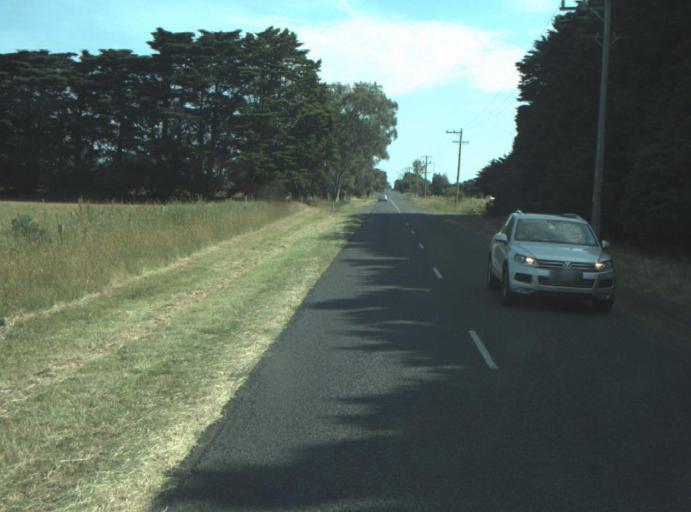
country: AU
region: Victoria
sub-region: Greater Geelong
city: Leopold
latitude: -38.1843
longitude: 144.5123
